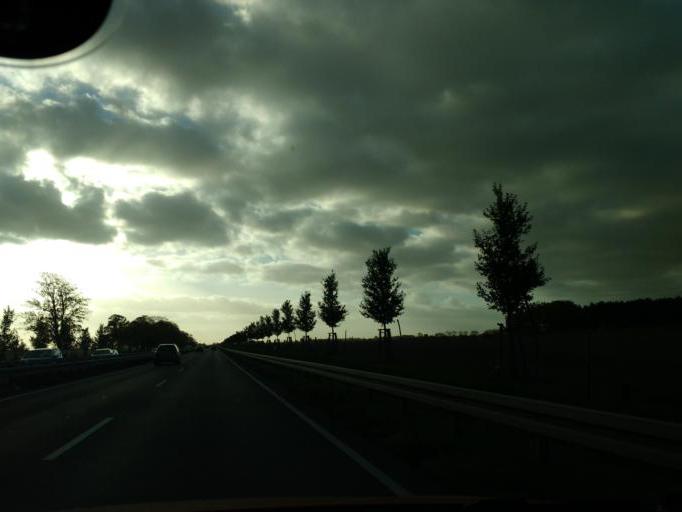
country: DE
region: Brandenburg
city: Hoppegarten
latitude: 52.5472
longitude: 13.6618
